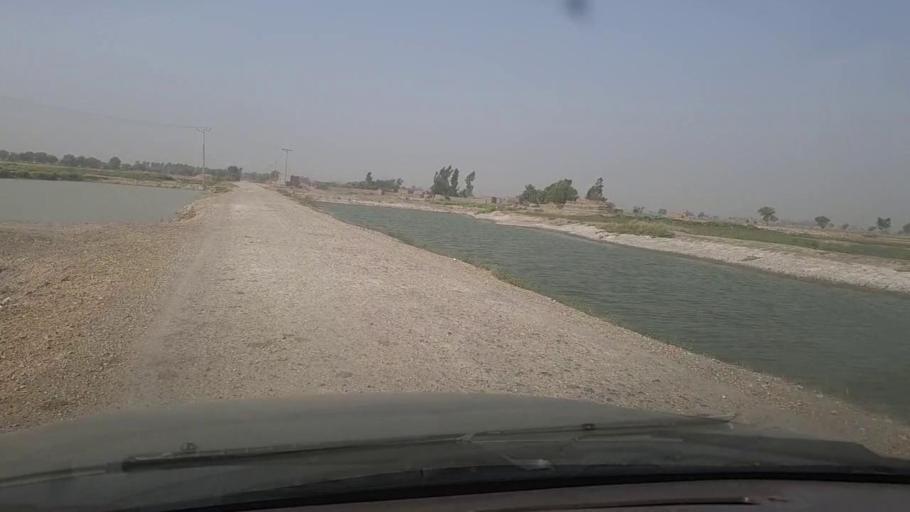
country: PK
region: Sindh
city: Garhi Yasin
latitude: 27.8793
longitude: 68.5671
